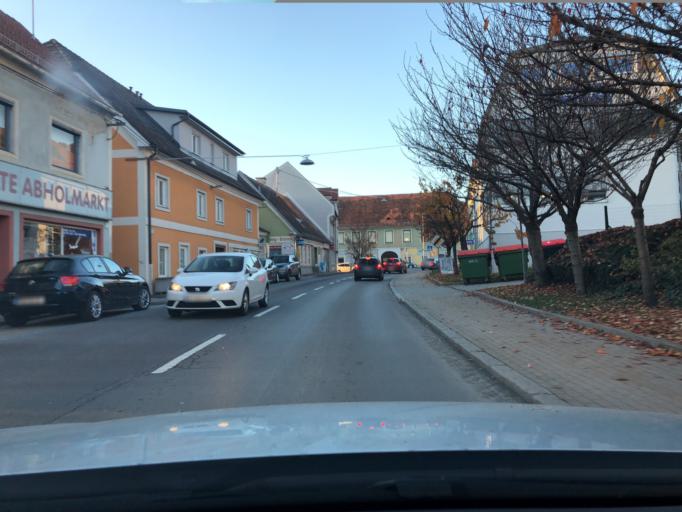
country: AT
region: Styria
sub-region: Politischer Bezirk Weiz
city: Gleisdorf
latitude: 47.1035
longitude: 15.7117
